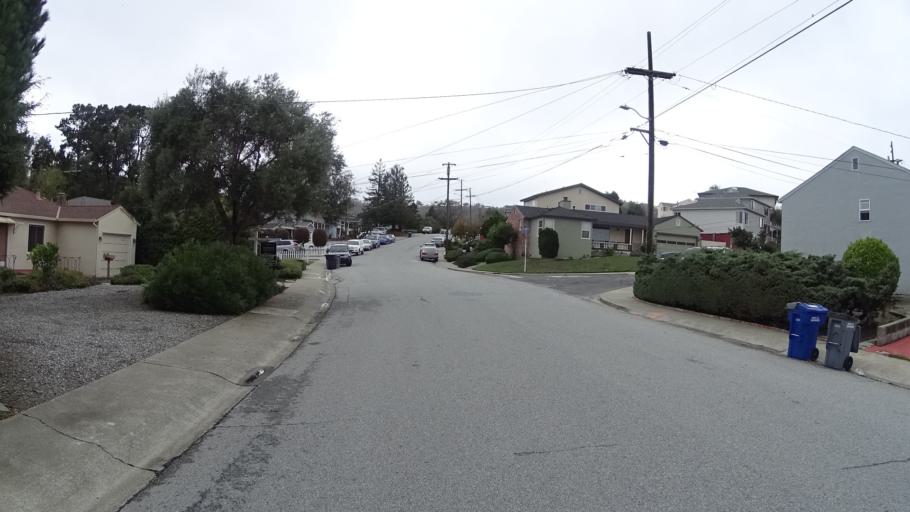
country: US
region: California
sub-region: San Mateo County
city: San Bruno
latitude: 37.6126
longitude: -122.4100
